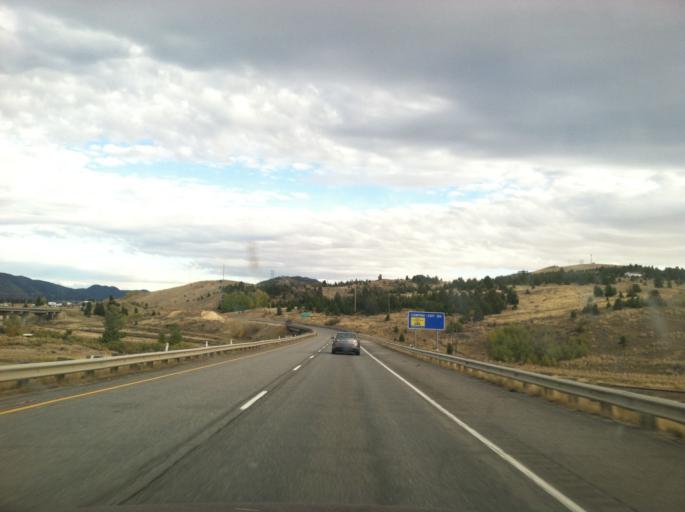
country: US
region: Montana
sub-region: Silver Bow County
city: Butte
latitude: 45.9988
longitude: -112.5682
